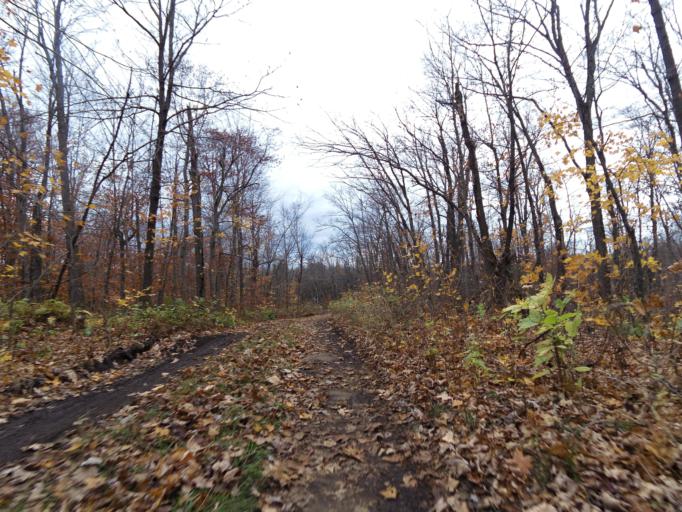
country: CA
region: Quebec
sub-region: Outaouais
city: Wakefield
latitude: 45.5555
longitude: -75.9781
